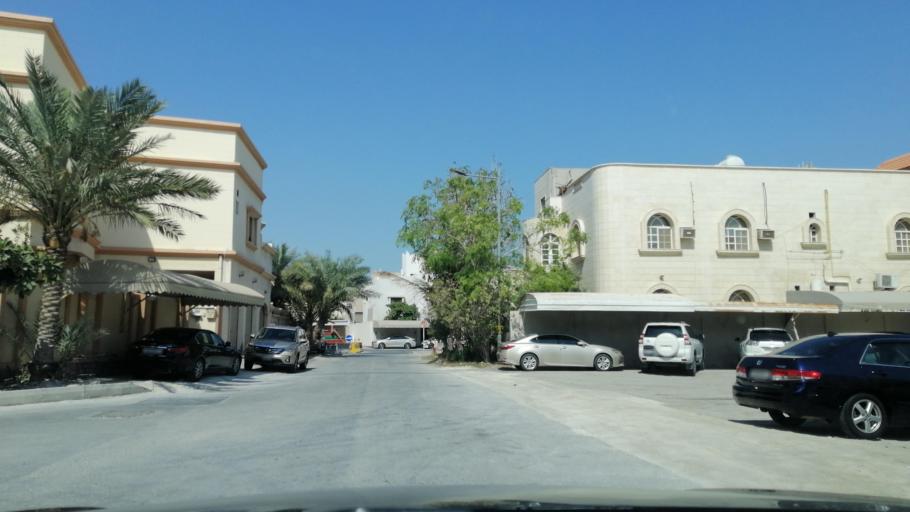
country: BH
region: Muharraq
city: Al Hadd
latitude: 26.2482
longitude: 50.6353
